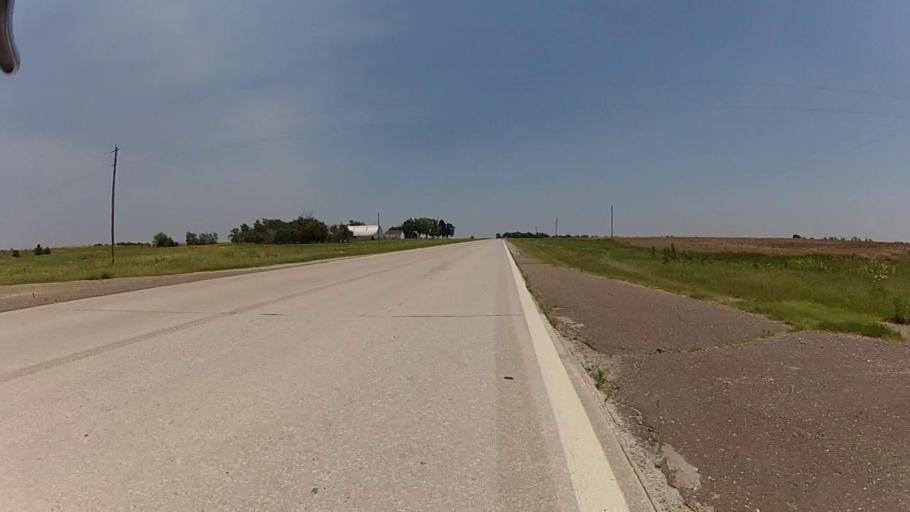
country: US
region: Kansas
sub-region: Sumner County
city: Wellington
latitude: 37.0572
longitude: -97.3650
